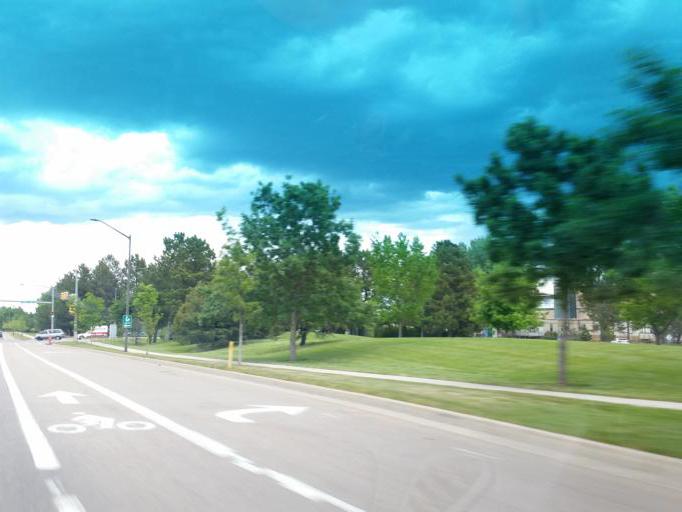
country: US
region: Colorado
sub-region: Larimer County
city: Fort Collins
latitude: 40.5253
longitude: -105.0202
